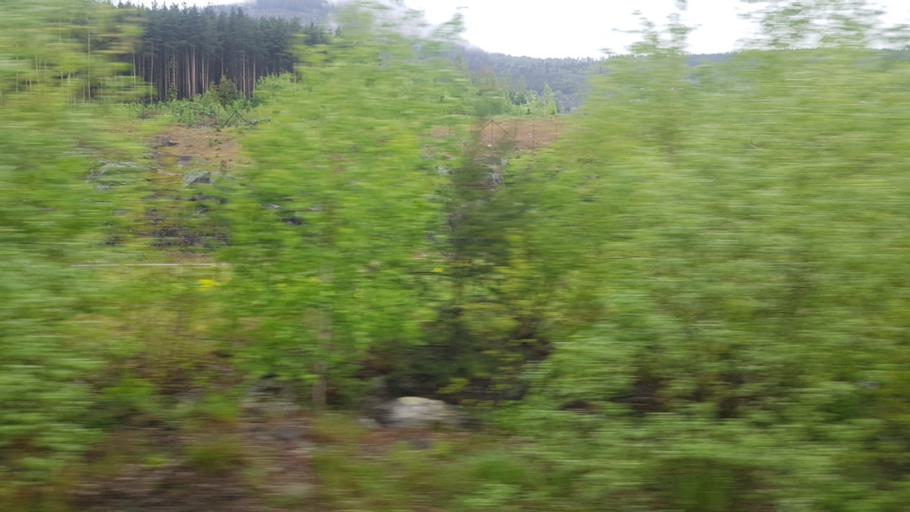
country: NO
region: Oppland
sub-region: Sor-Fron
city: Hundorp
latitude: 61.5712
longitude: 9.8653
